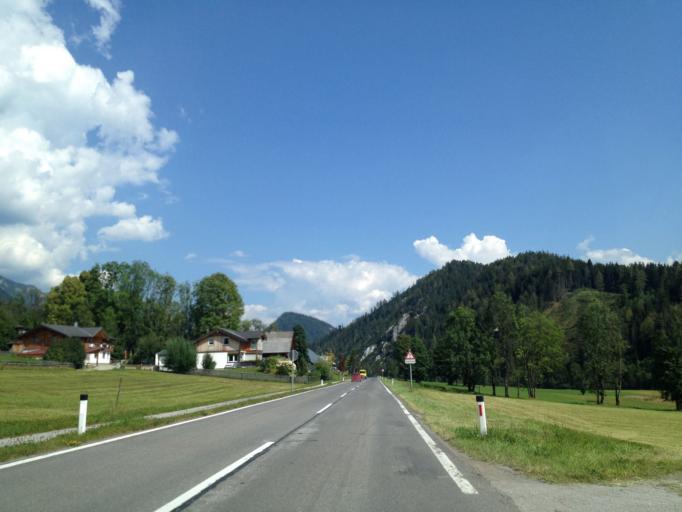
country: AT
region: Styria
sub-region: Politischer Bezirk Liezen
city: Schladming
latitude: 47.4241
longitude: 13.6889
